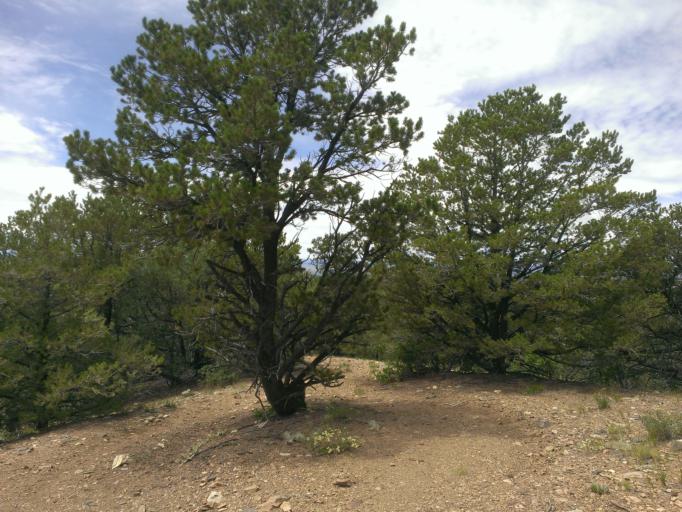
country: US
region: New Mexico
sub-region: Taos County
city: Arroyo Seco
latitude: 36.5358
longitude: -105.5576
